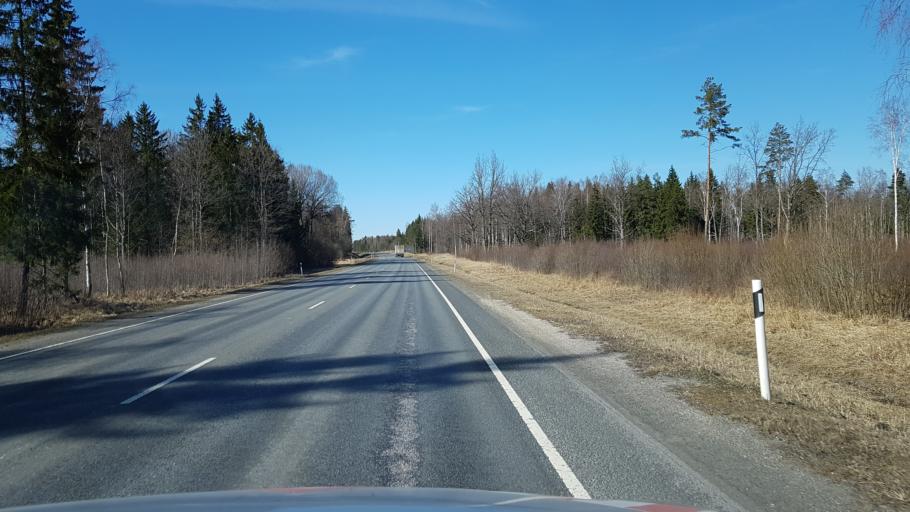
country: EE
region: Harju
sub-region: Nissi vald
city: Turba
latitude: 58.9481
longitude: 24.0839
